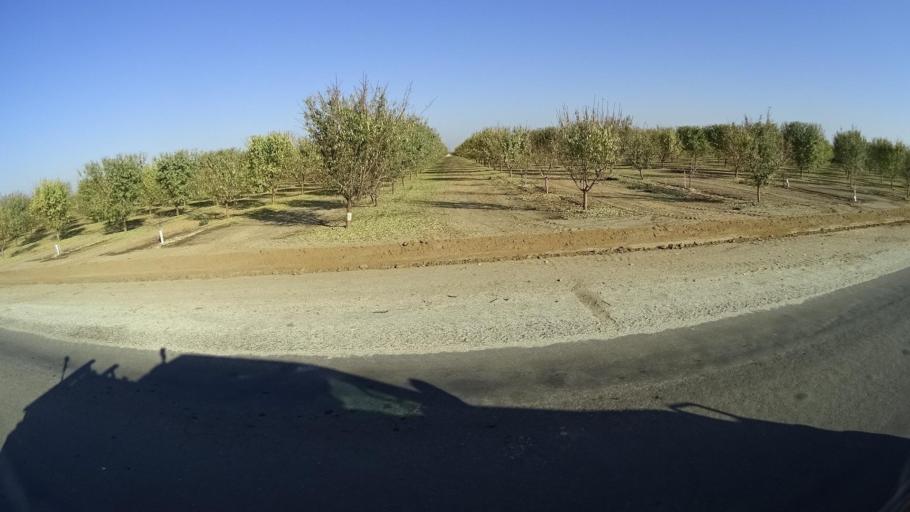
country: US
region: California
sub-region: Tulare County
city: Richgrove
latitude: 35.7687
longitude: -119.1719
